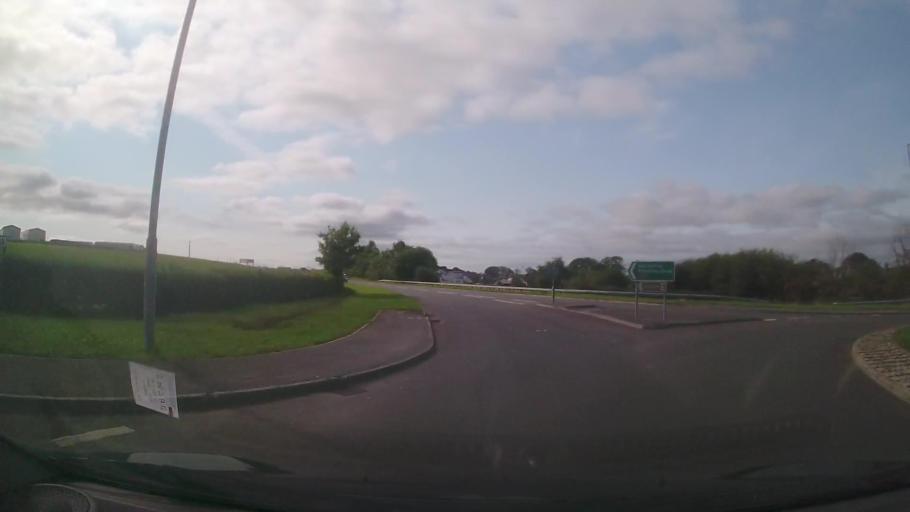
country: GB
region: Wales
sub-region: Pembrokeshire
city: Manorbier
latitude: 51.6939
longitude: -4.8091
